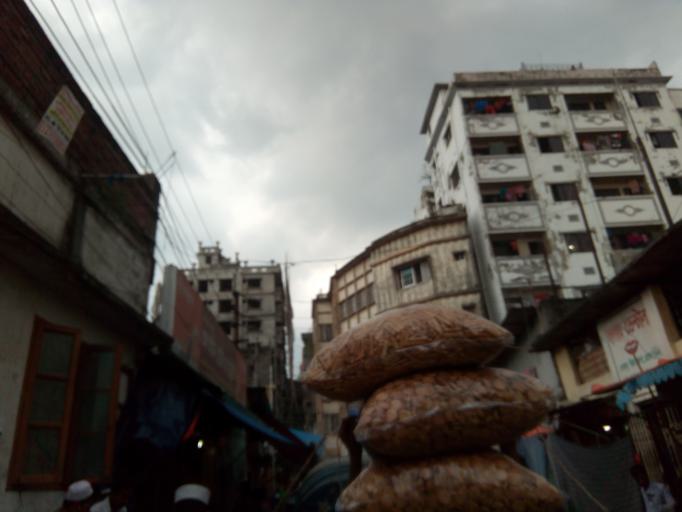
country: BD
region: Dhaka
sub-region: Dhaka
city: Dhaka
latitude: 23.7139
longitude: 90.3944
